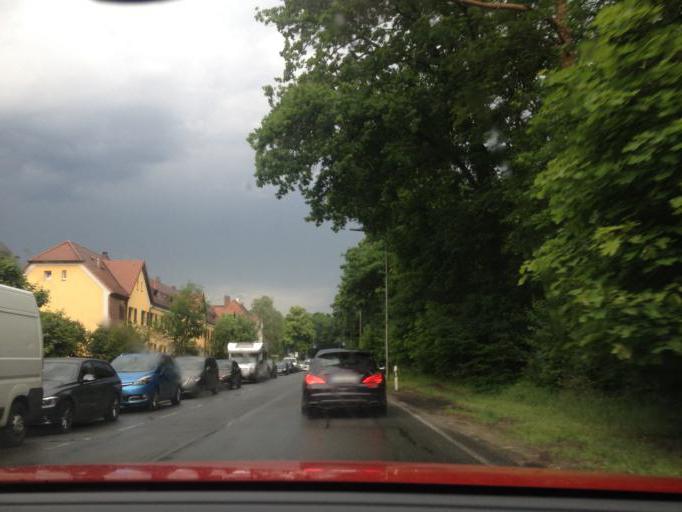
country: DE
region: Bavaria
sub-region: Regierungsbezirk Mittelfranken
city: Nuernberg
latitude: 49.4478
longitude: 11.1297
